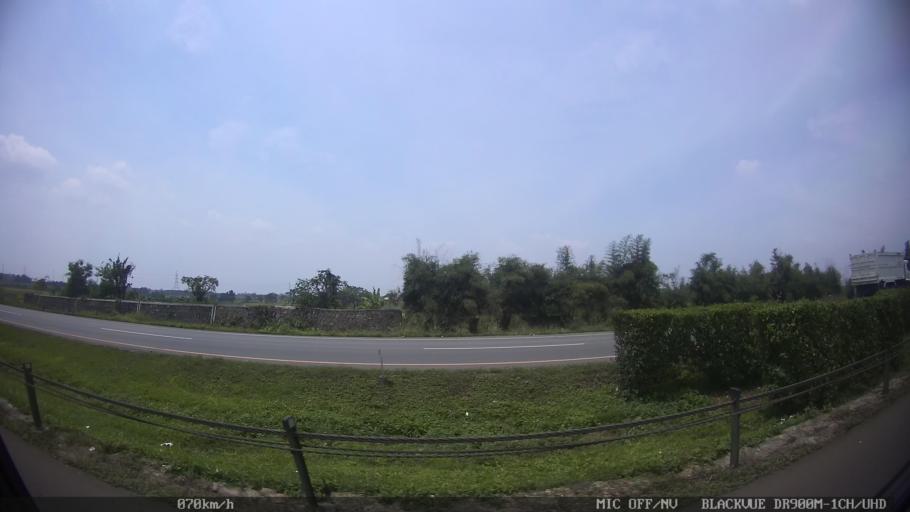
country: ID
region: West Java
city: Kresek
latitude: -6.1567
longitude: 106.3243
